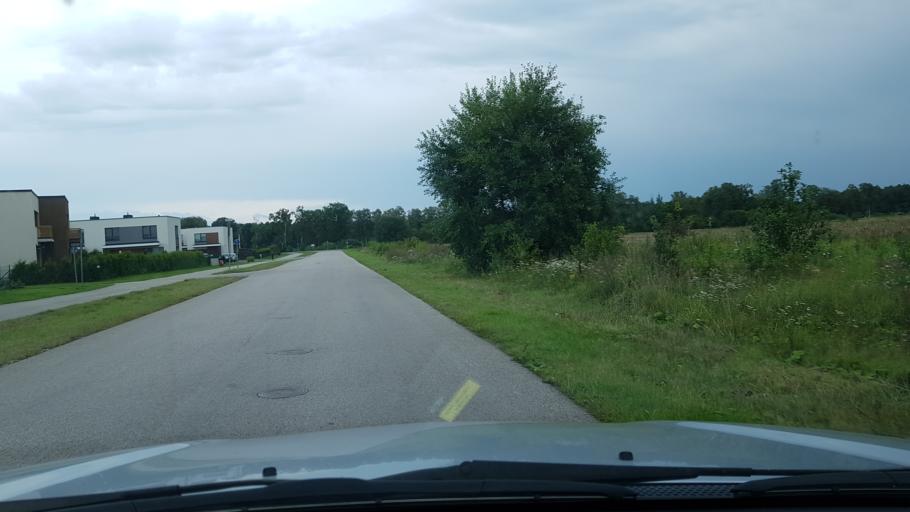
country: EE
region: Harju
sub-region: Rae vald
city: Jueri
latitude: 59.3478
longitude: 24.8995
